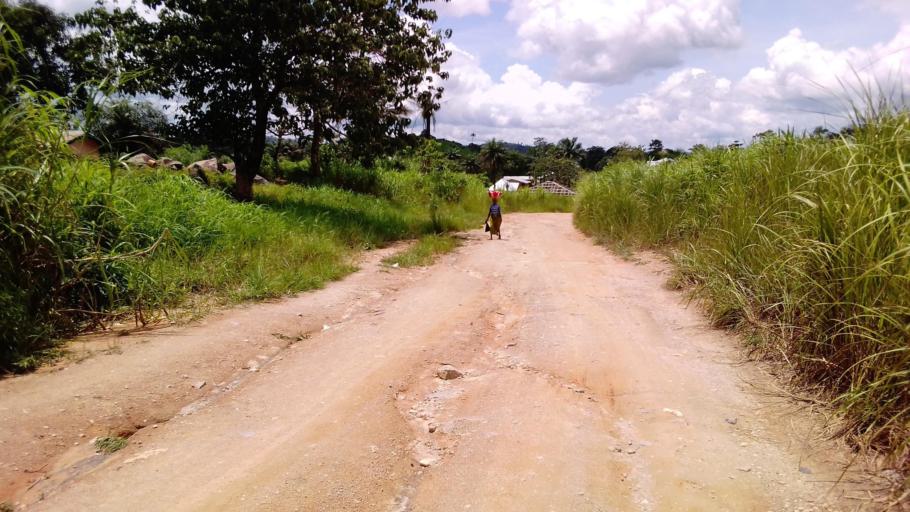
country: SL
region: Eastern Province
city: Koidu
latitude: 8.6661
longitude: -10.9718
